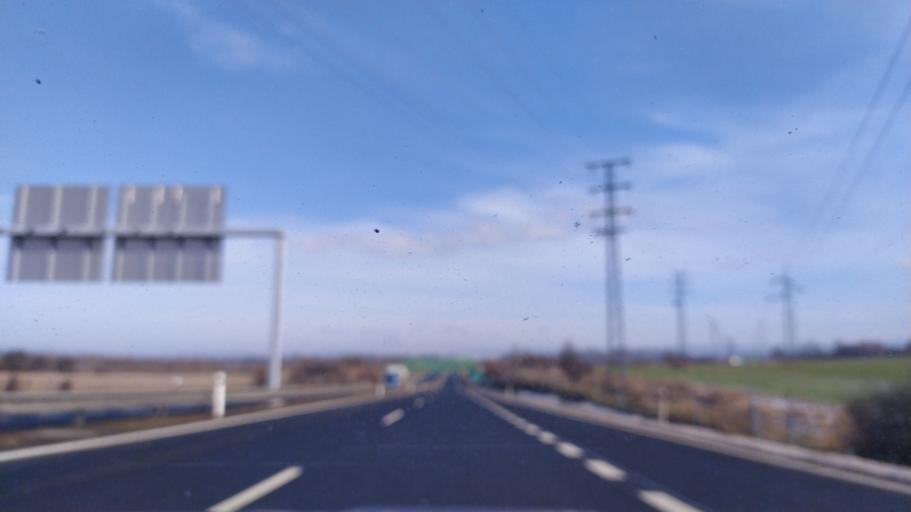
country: CZ
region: Karlovarsky
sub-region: Okres Cheb
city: Cheb
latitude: 50.0986
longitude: 12.3754
